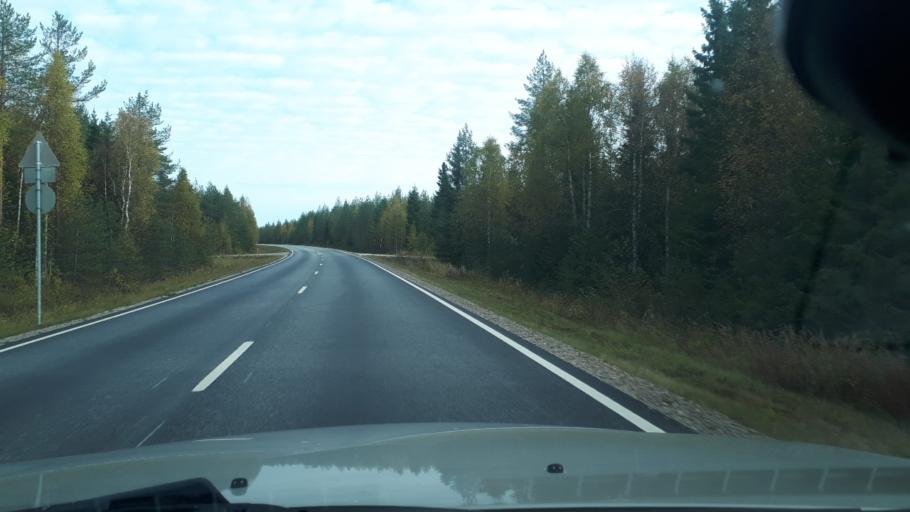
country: FI
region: Northern Ostrobothnia
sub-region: Oulu
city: Yli-Ii
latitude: 65.9015
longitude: 25.7317
